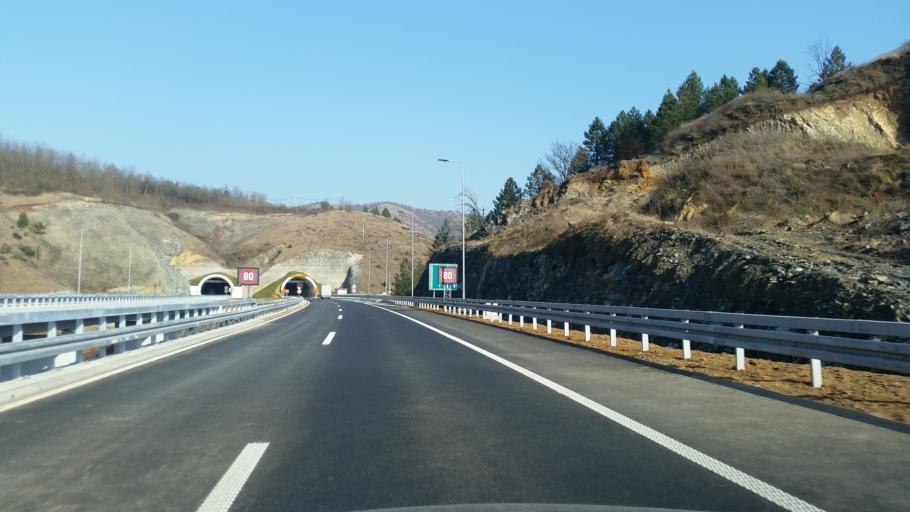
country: RS
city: Prislonica
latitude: 43.9753
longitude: 20.3992
